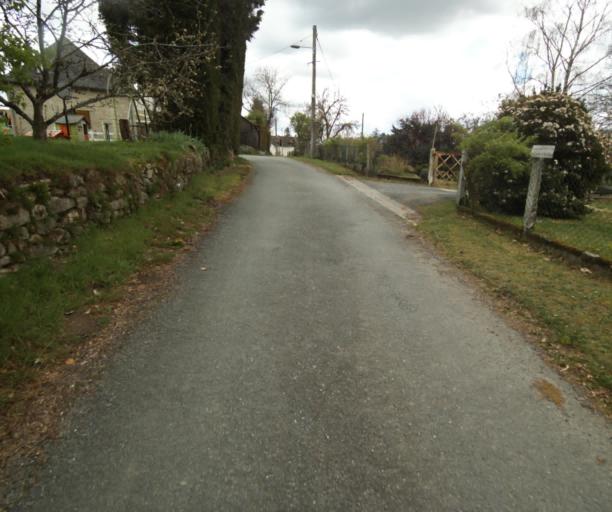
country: FR
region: Limousin
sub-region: Departement de la Correze
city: Correze
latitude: 45.3162
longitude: 1.8808
